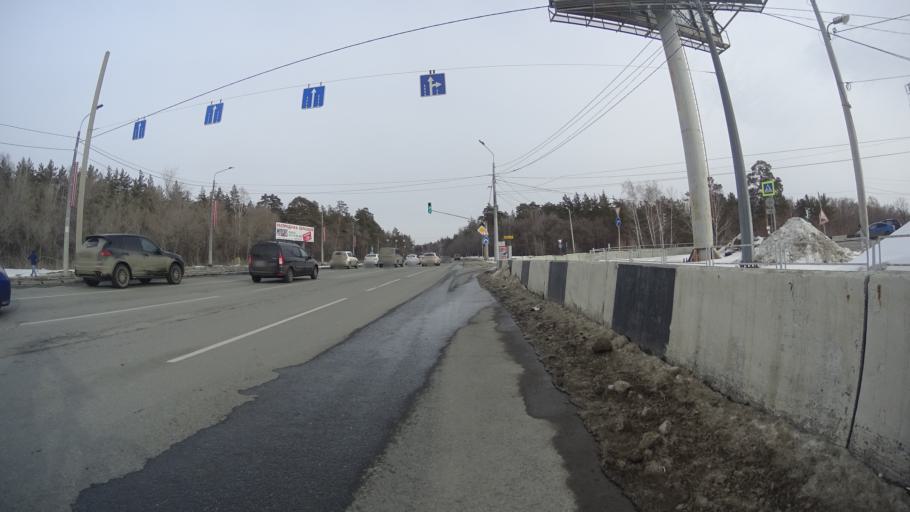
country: RU
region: Chelyabinsk
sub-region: Gorod Chelyabinsk
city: Chelyabinsk
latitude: 55.1473
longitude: 61.3287
